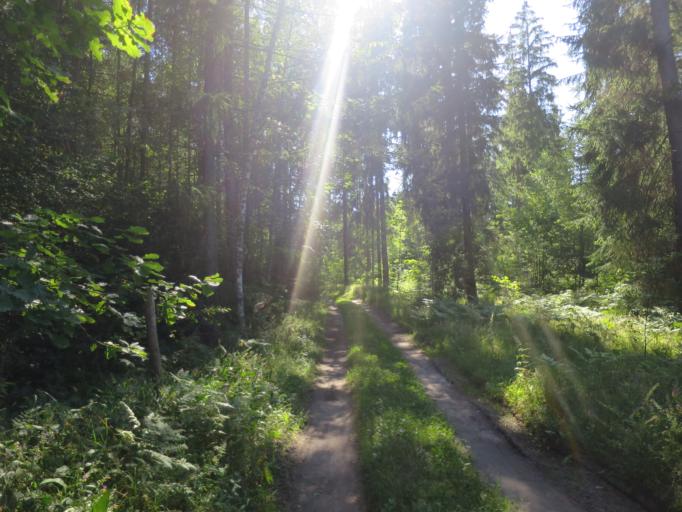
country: LV
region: Sigulda
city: Sigulda
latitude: 57.1068
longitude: 24.8122
